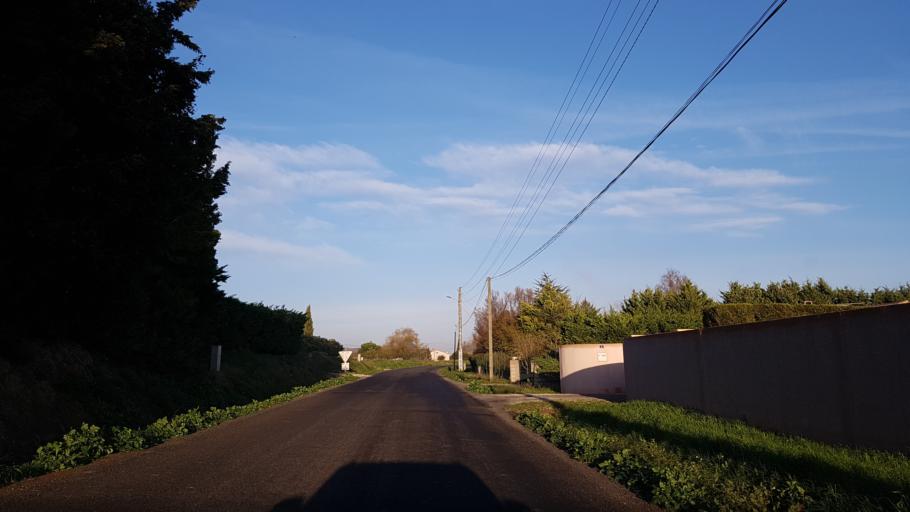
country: FR
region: Languedoc-Roussillon
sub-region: Departement de l'Aude
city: Villeneuve-la-Comptal
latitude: 43.2758
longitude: 1.9445
